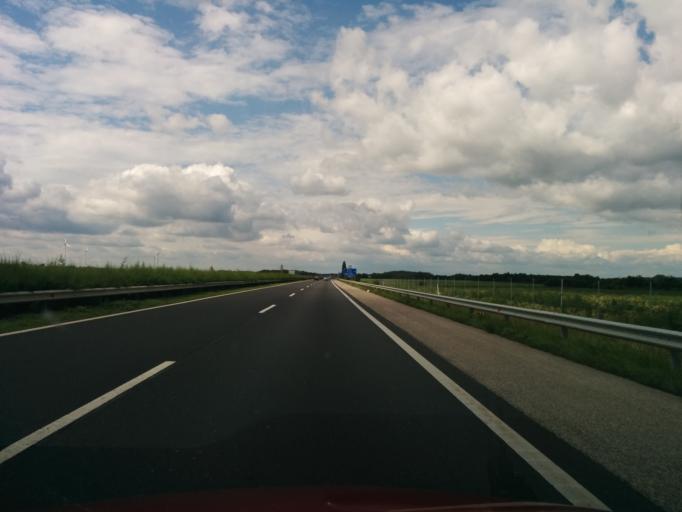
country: HU
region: Gyor-Moson-Sopron
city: Bony
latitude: 47.6809
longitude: 17.9107
